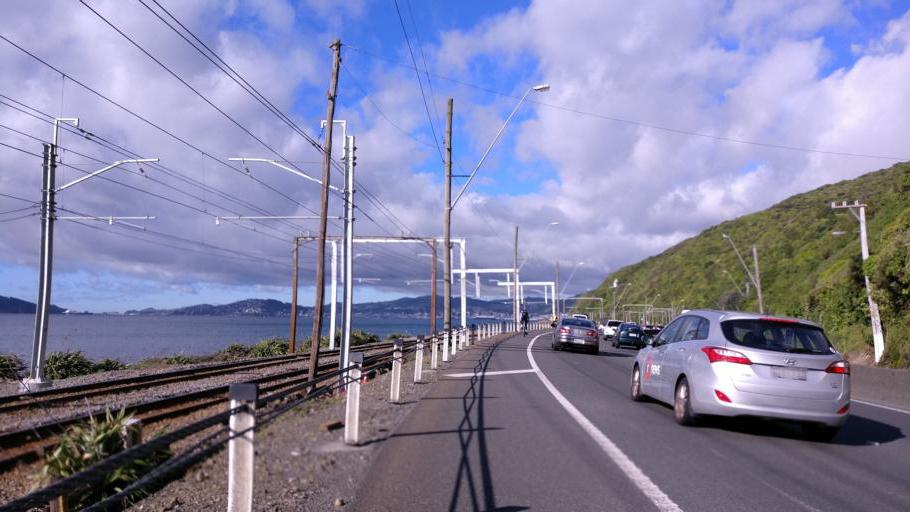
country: NZ
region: Wellington
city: Petone
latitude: -41.2309
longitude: 174.8411
